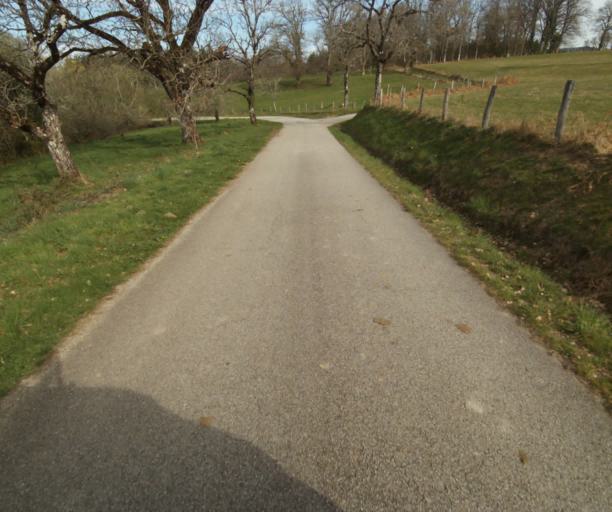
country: FR
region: Limousin
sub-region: Departement de la Correze
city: Correze
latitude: 45.4180
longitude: 1.8149
